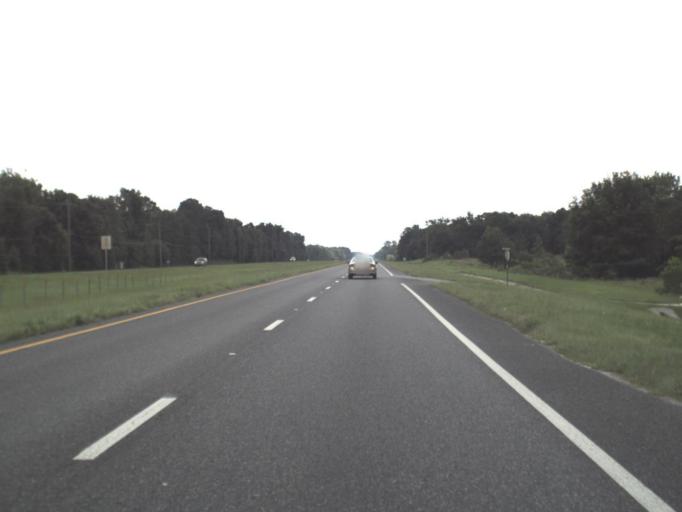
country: US
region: Florida
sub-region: Levy County
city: Williston Highlands
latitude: 29.4085
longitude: -82.5327
